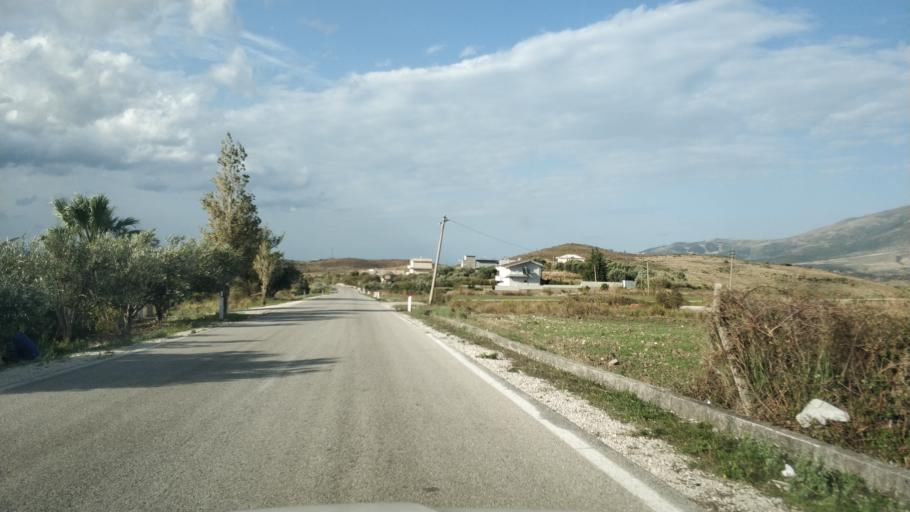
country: AL
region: Vlore
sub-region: Rrethi i Vlores
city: Orikum
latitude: 40.3067
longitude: 19.4819
